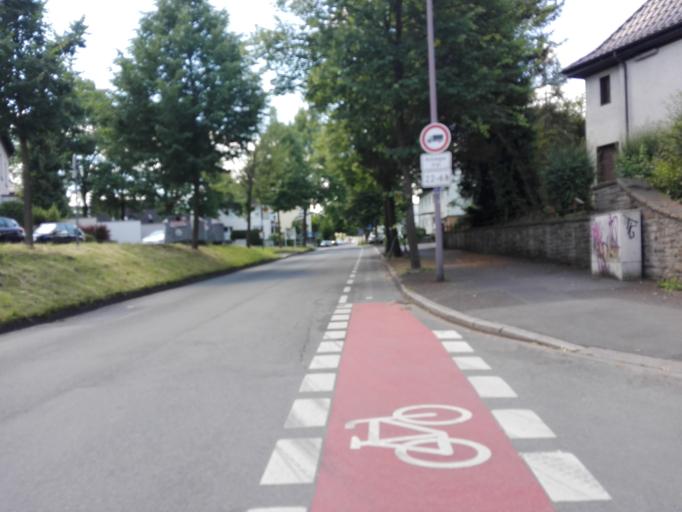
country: DE
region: North Rhine-Westphalia
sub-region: Regierungsbezirk Arnsberg
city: Unna
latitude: 51.5373
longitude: 7.6978
